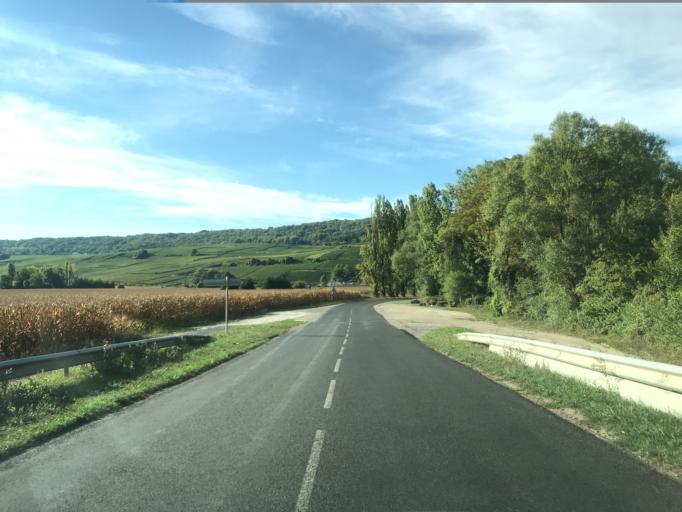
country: FR
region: Champagne-Ardenne
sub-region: Departement de la Marne
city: Mareuil-le-Port
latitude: 49.0805
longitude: 3.7963
